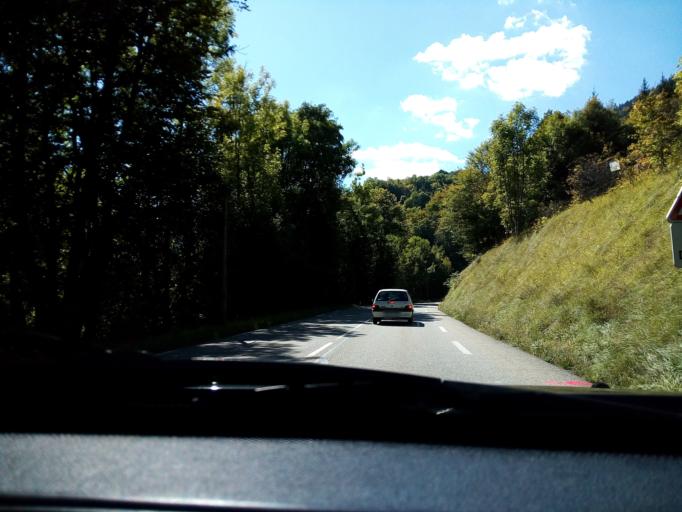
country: FR
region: Rhone-Alpes
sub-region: Departement de l'Isere
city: Sassenage
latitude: 45.1875
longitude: 5.6228
